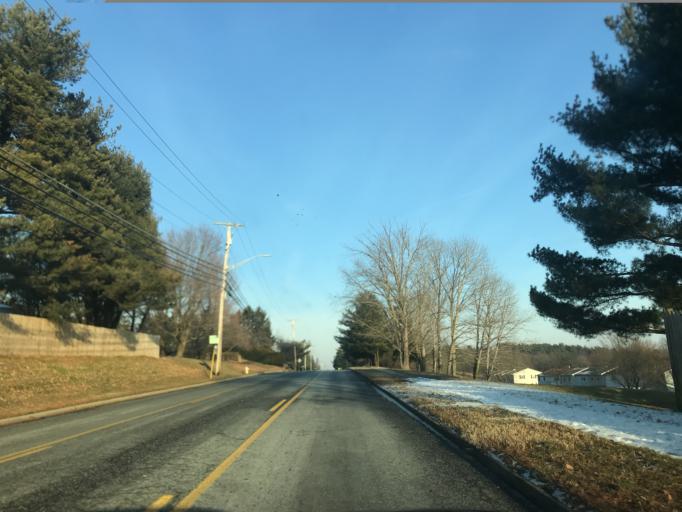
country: US
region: Maryland
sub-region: Harford County
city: Edgewood
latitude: 39.4230
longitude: -76.3216
